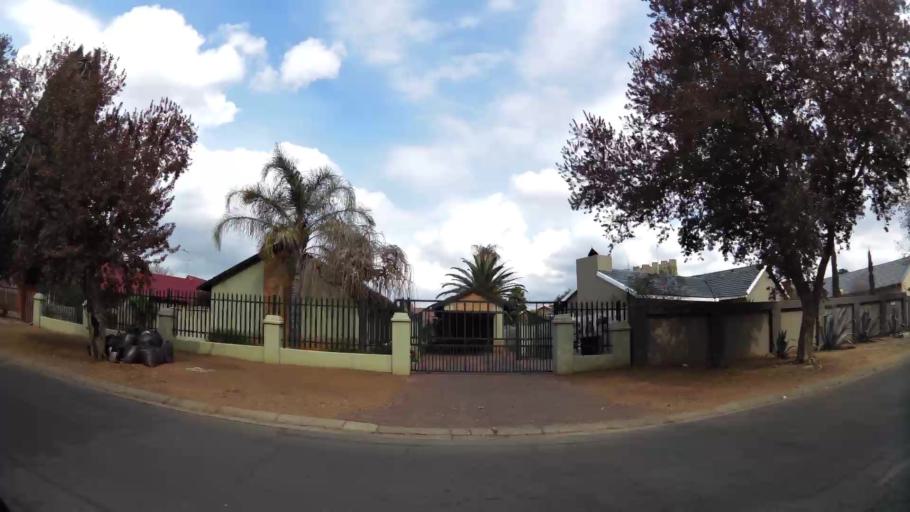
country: ZA
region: Gauteng
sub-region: Sedibeng District Municipality
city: Vanderbijlpark
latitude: -26.7247
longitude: 27.8512
